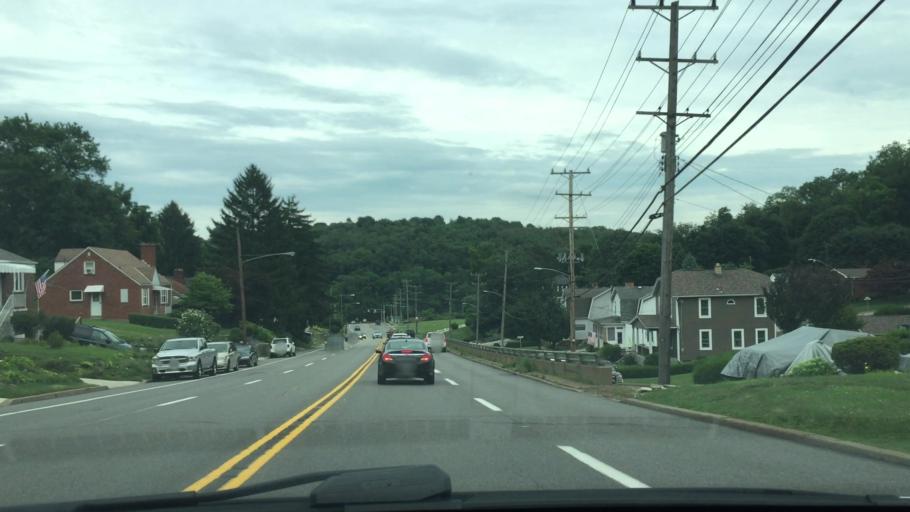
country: US
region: Pennsylvania
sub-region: Allegheny County
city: Castle Shannon
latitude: 40.3551
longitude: -80.0337
